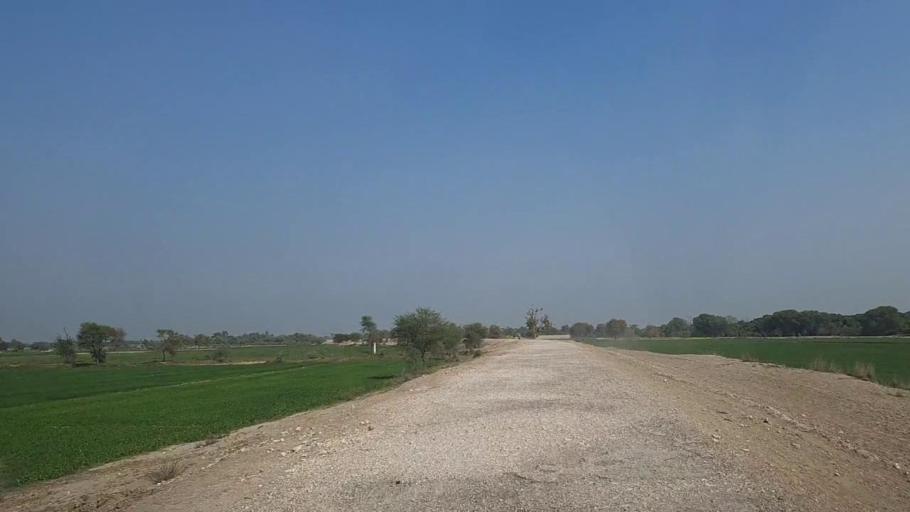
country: PK
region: Sindh
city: Moro
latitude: 26.7982
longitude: 67.9415
